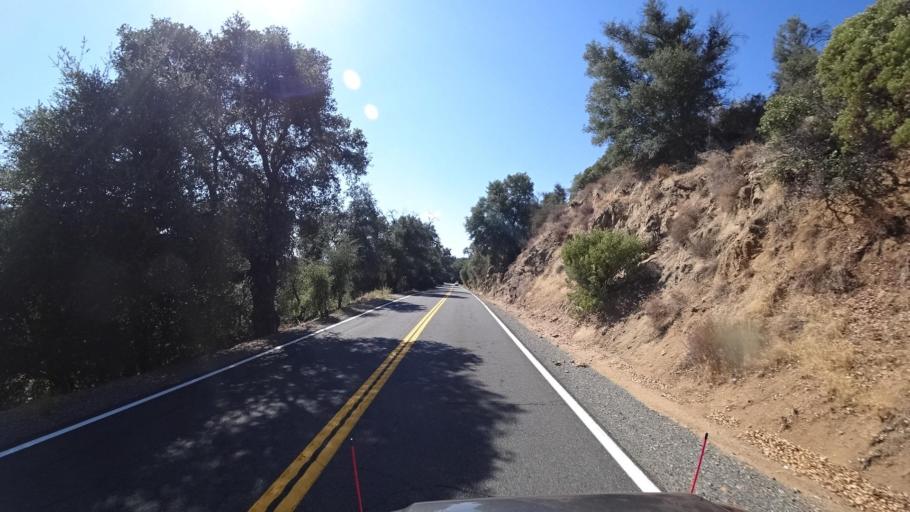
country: US
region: California
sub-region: Riverside County
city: Aguanga
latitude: 33.3209
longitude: -116.6988
